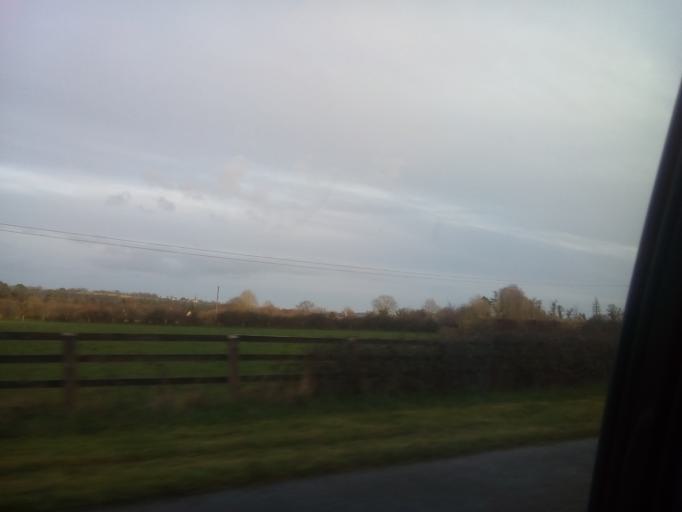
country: IE
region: Leinster
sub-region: Laois
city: Abbeyleix
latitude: 52.8836
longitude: -7.3644
